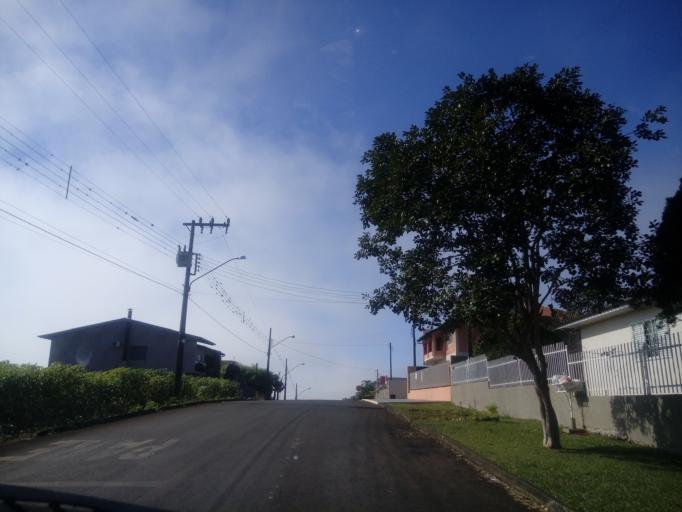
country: BR
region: Santa Catarina
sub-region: Chapeco
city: Chapeco
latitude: -27.0756
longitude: -52.6143
